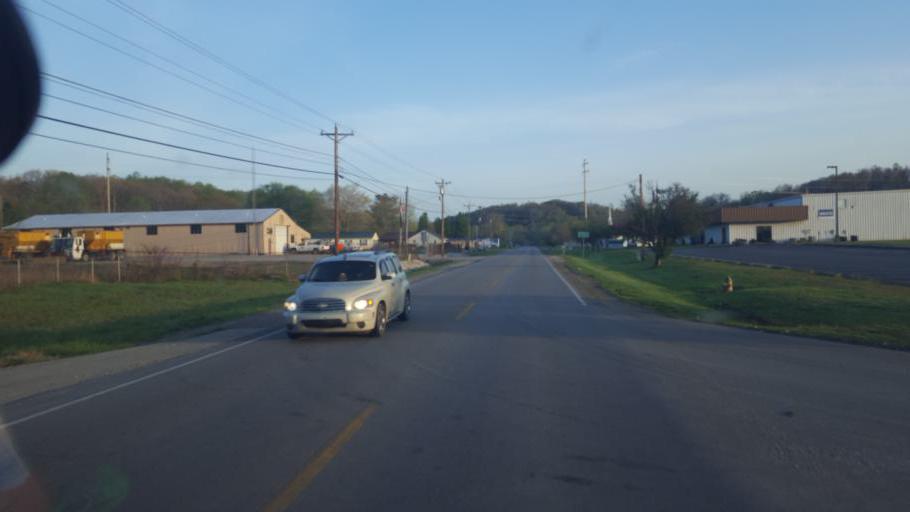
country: US
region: Kentucky
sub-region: Hart County
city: Munfordville
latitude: 37.2955
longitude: -85.9066
